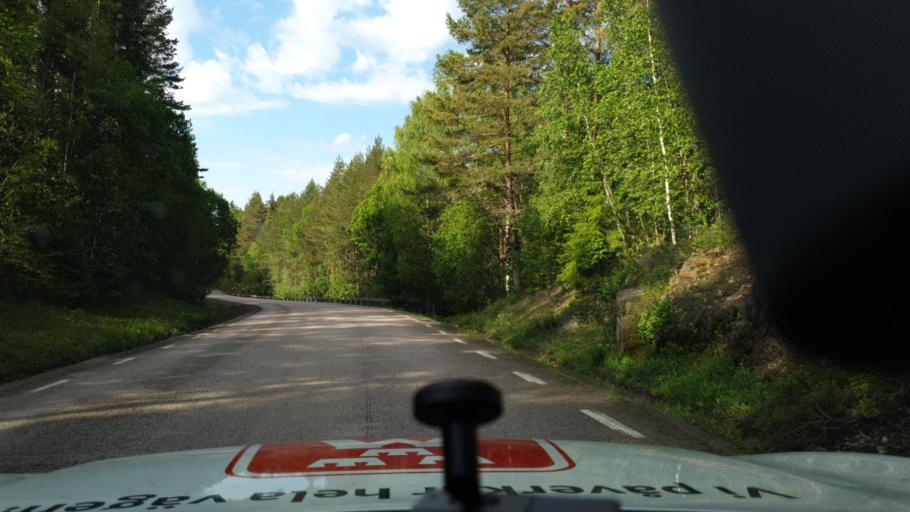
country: SE
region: Vaermland
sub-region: Arvika Kommun
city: Arvika
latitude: 59.9157
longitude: 12.6472
